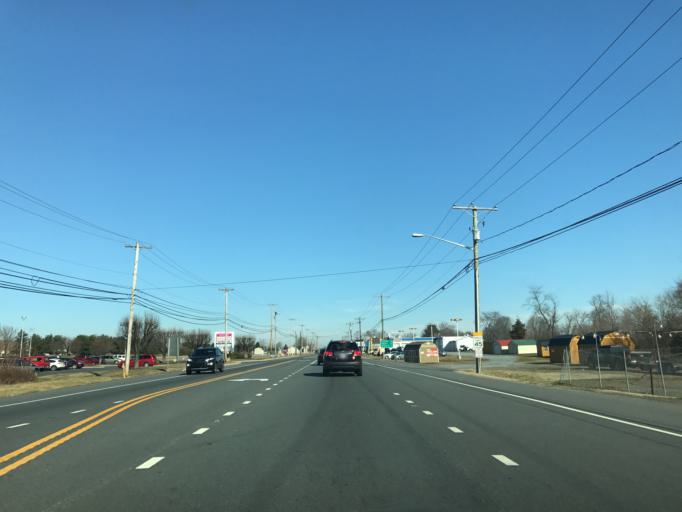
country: US
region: Delaware
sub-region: New Castle County
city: Middletown
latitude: 39.4644
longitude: -75.7213
